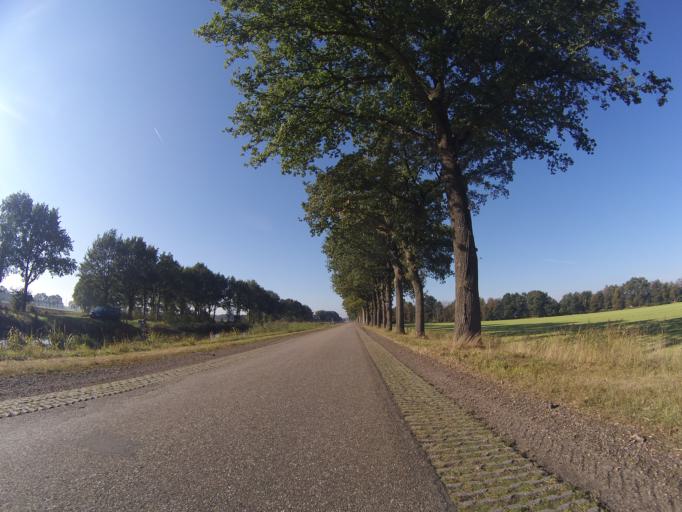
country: NL
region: Drenthe
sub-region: Gemeente Coevorden
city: Dalen
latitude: 52.7392
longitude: 6.7391
